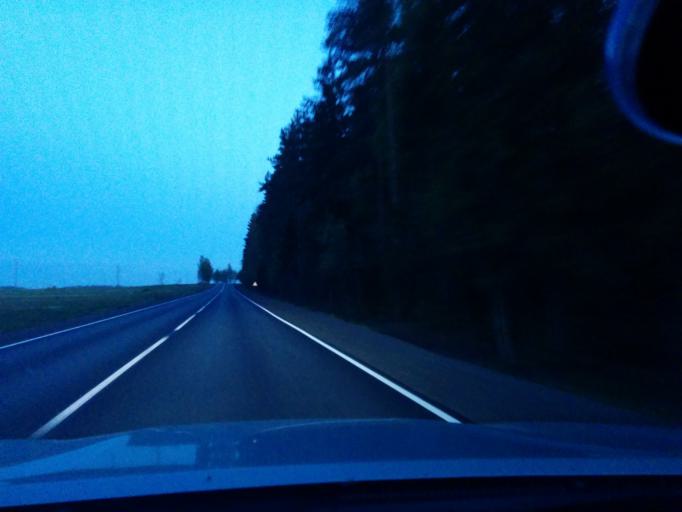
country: RU
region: Leningrad
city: Verkhniye Osel'ki
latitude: 60.1920
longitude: 30.4139
